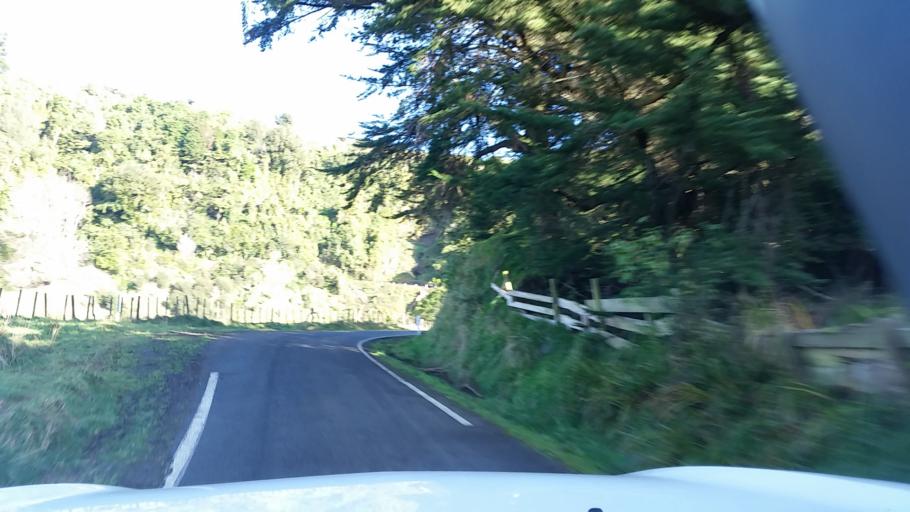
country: NZ
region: Taranaki
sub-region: South Taranaki District
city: Eltham
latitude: -39.5118
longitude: 174.3838
